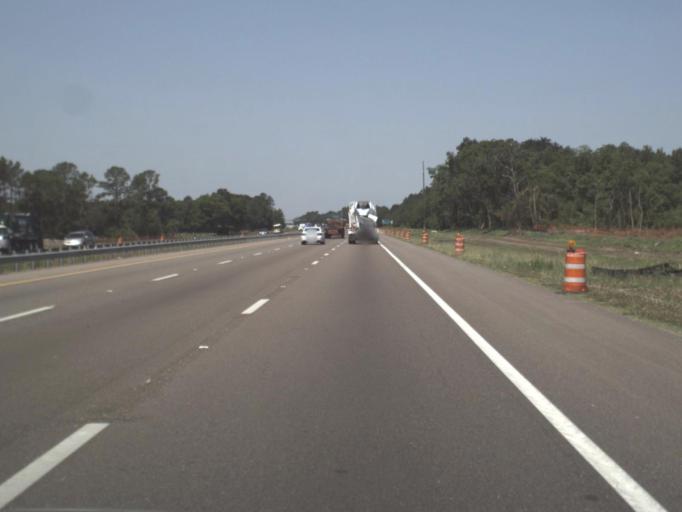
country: US
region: Florida
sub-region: Duval County
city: Jacksonville
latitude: 30.3150
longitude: -81.7933
